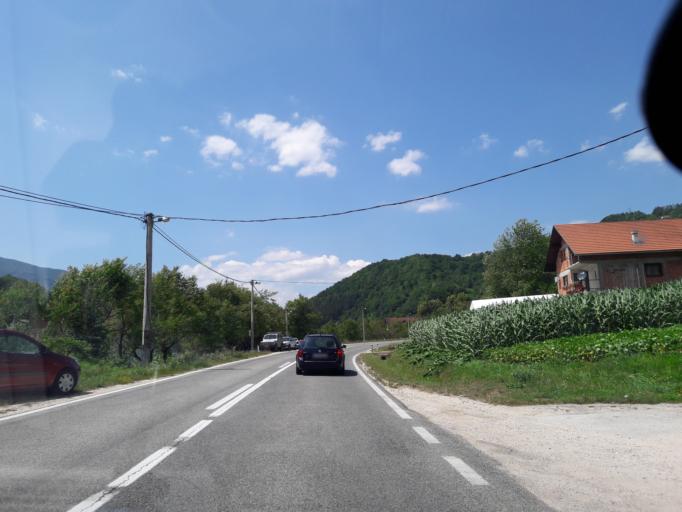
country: BA
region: Republika Srpska
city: Mrkonjic Grad
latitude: 44.3721
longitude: 17.1404
